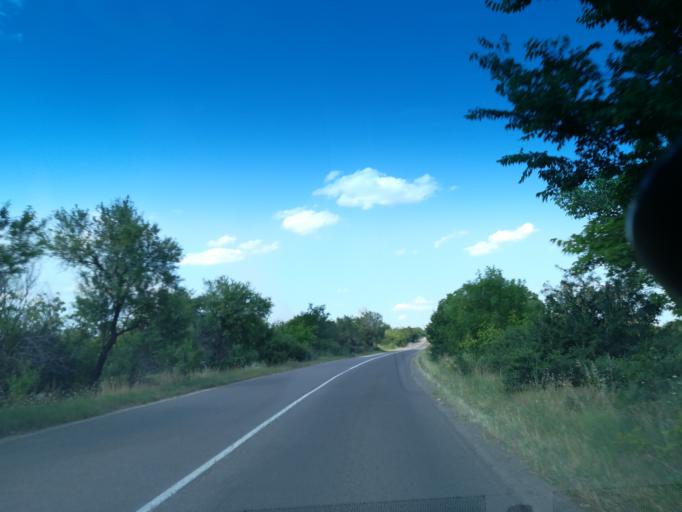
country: BG
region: Stara Zagora
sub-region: Obshtina Chirpan
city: Chirpan
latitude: 42.2146
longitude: 25.3694
